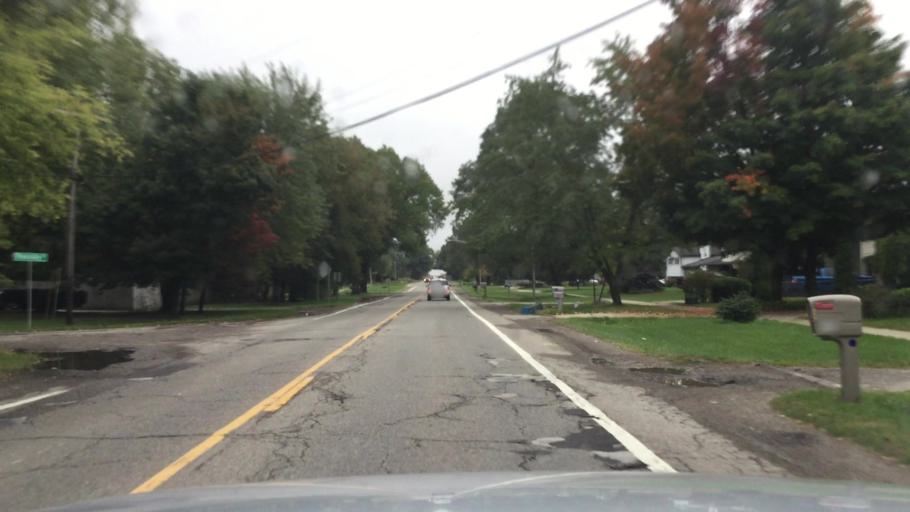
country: US
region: Michigan
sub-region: Oakland County
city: Waterford
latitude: 42.6809
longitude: -83.4069
